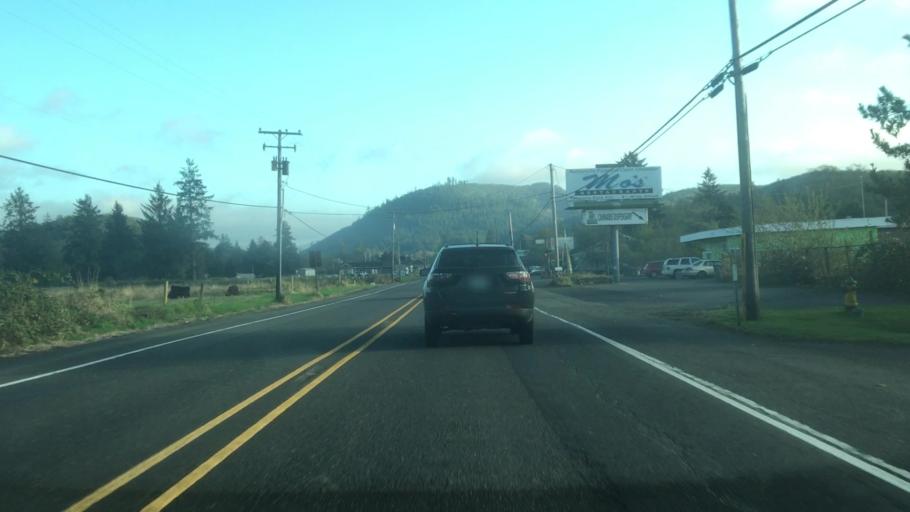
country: US
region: Oregon
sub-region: Clatsop County
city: Seaside
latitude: 45.9455
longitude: -123.9221
